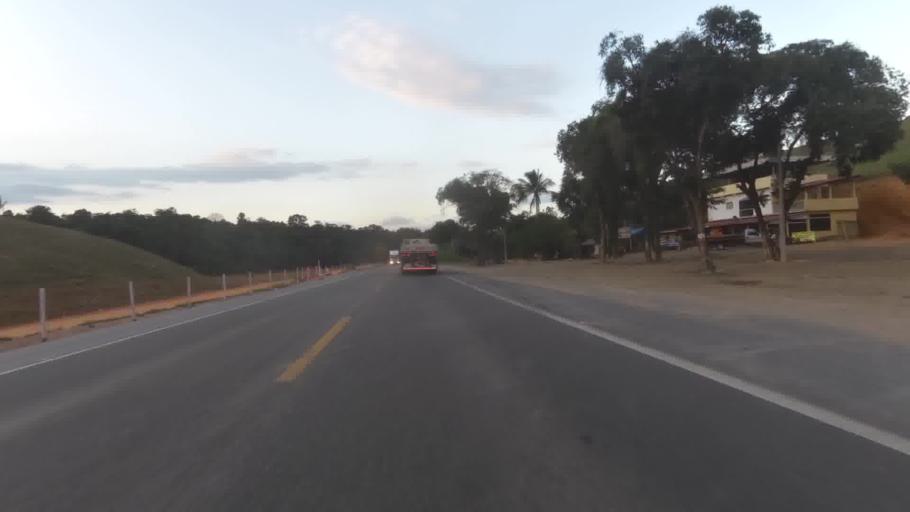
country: BR
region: Espirito Santo
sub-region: Alfredo Chaves
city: Alfredo Chaves
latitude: -20.7235
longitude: -40.7398
